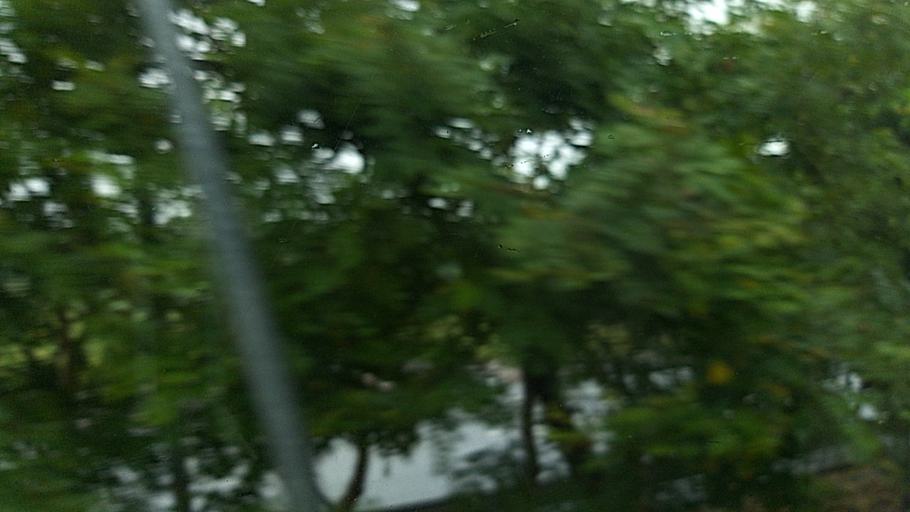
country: TH
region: Nakhon Ratchasima
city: Phimai
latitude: 15.2622
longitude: 102.4176
